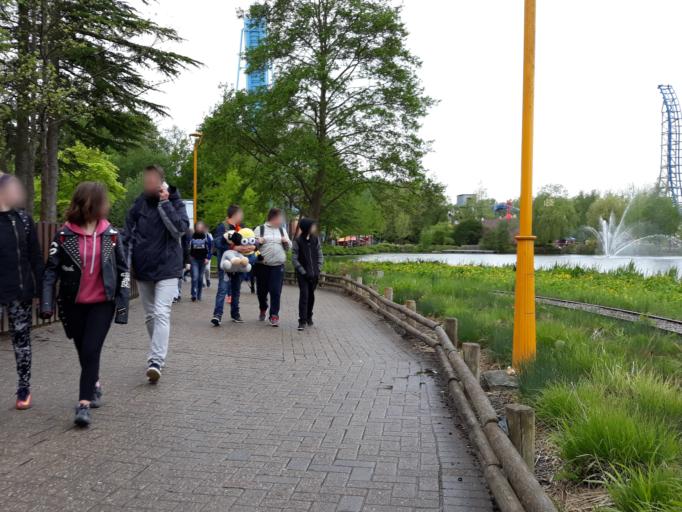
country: BE
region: Wallonia
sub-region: Province du Brabant Wallon
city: Wavre
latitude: 50.6989
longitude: 4.5925
